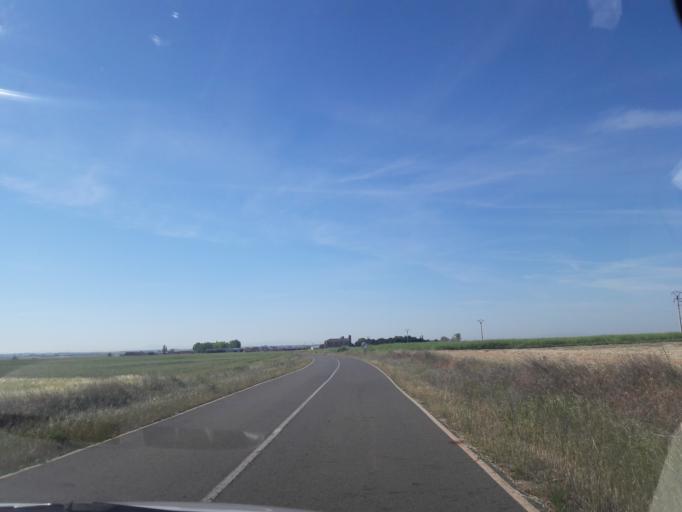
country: ES
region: Castille and Leon
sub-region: Provincia de Salamanca
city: Arcediano
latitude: 41.1013
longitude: -5.5657
